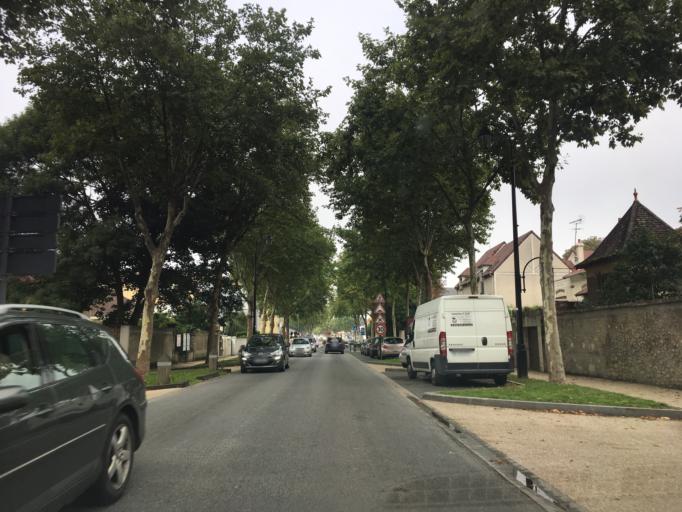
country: FR
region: Ile-de-France
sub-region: Departement de Seine-et-Marne
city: Brie-Comte-Robert
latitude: 48.6952
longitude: 2.6092
